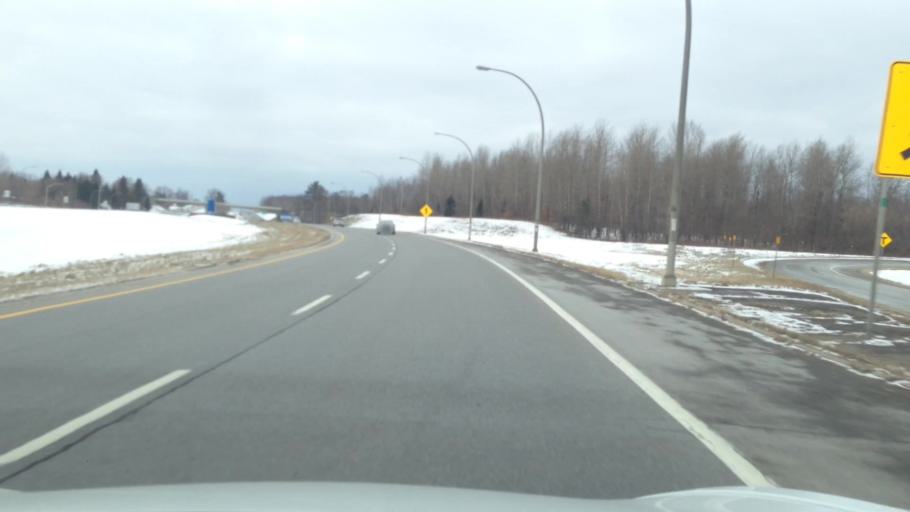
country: CA
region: Quebec
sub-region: Monteregie
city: Rigaud
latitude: 45.5373
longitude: -74.3828
